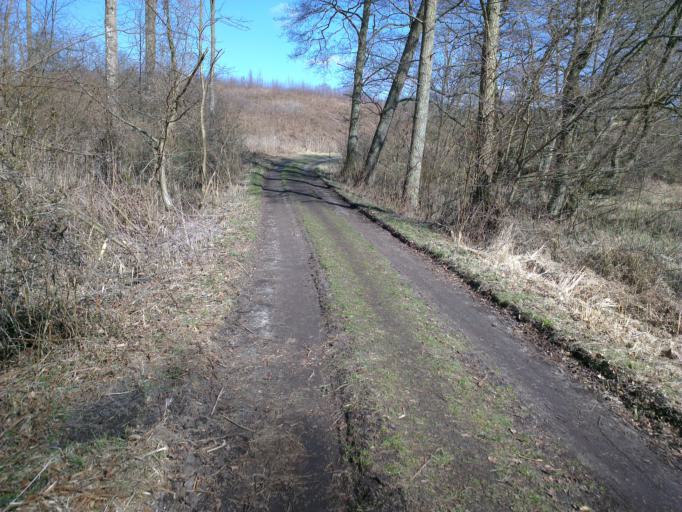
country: DK
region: Capital Region
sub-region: Frederikssund Kommune
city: Jaegerspris
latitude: 55.9263
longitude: 11.9405
